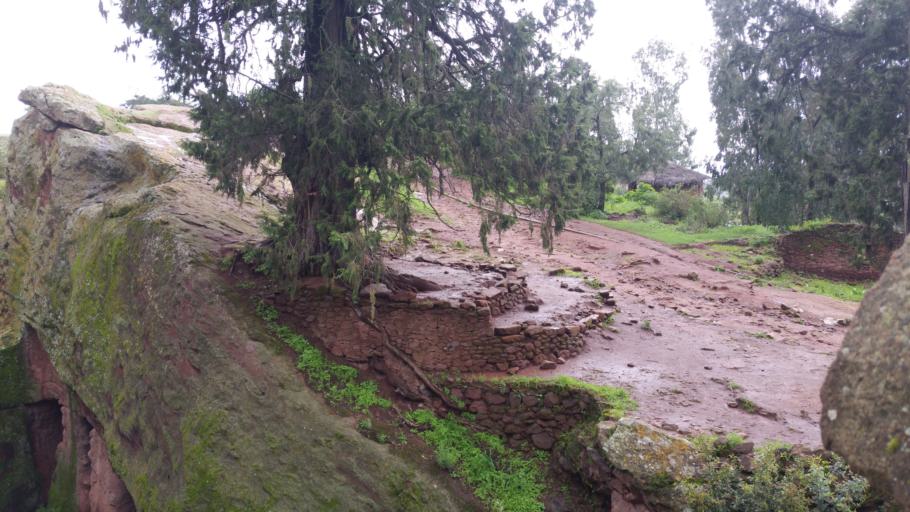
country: ET
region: Amhara
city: Lalibela
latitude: 12.0315
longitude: 39.0446
